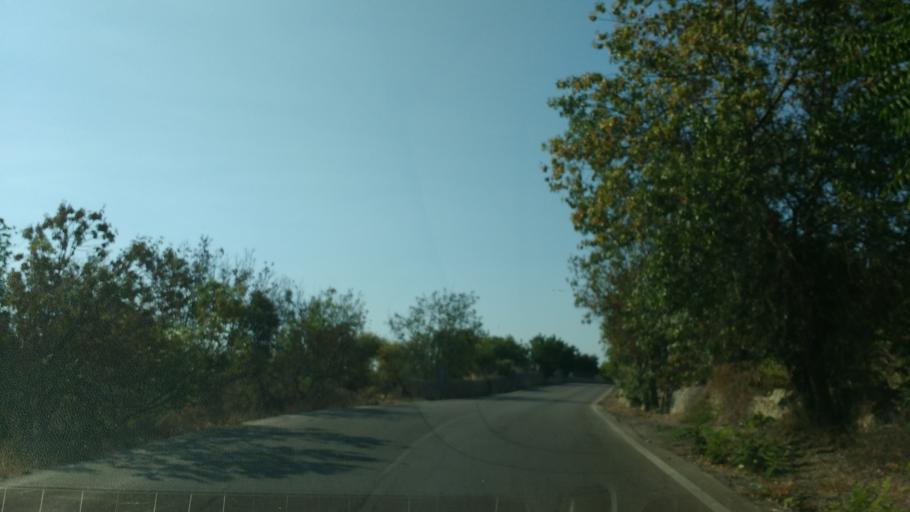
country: ES
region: Balearic Islands
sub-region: Illes Balears
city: Consell
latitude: 39.6806
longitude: 2.8124
